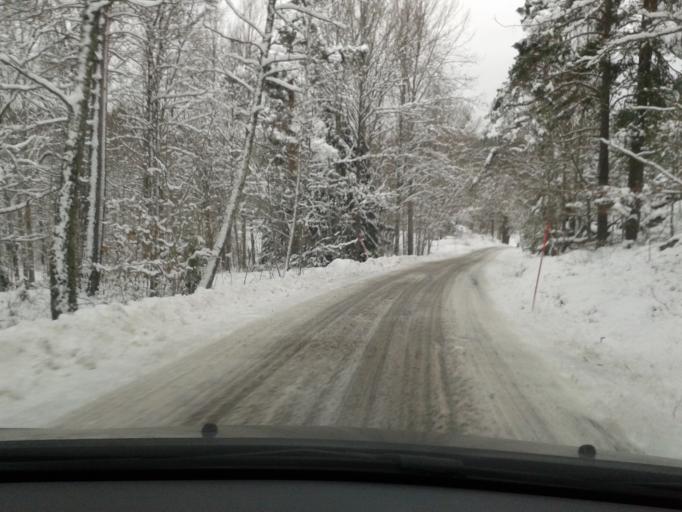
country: SE
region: Stockholm
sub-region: Tyreso Kommun
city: Brevik
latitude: 59.2049
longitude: 18.3182
